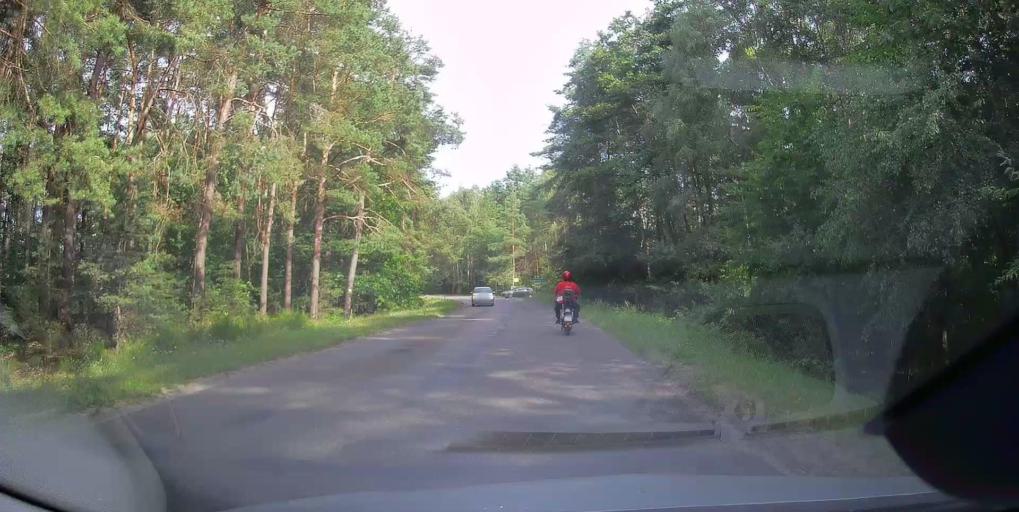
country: PL
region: Lodz Voivodeship
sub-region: Powiat tomaszowski
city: Tomaszow Mazowiecki
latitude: 51.4744
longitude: 19.9887
